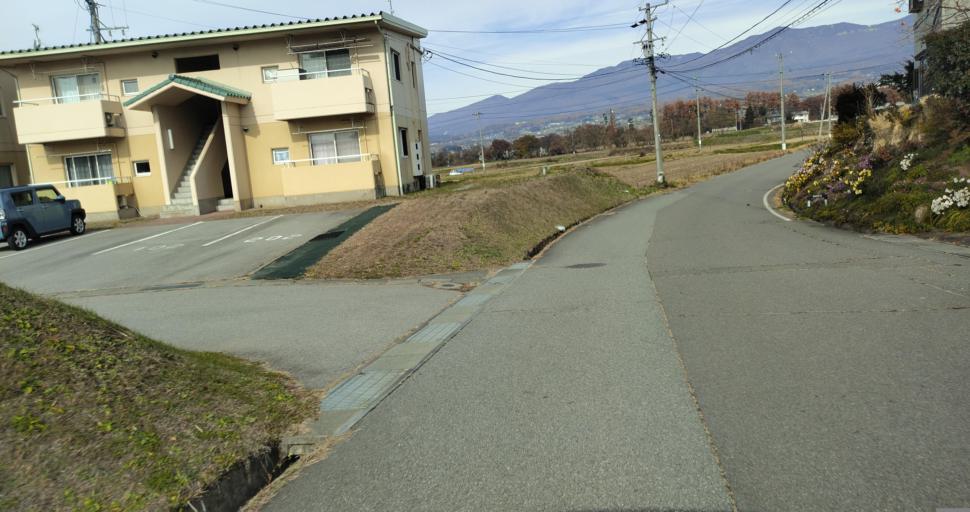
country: JP
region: Nagano
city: Komoro
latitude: 36.3038
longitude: 138.4726
